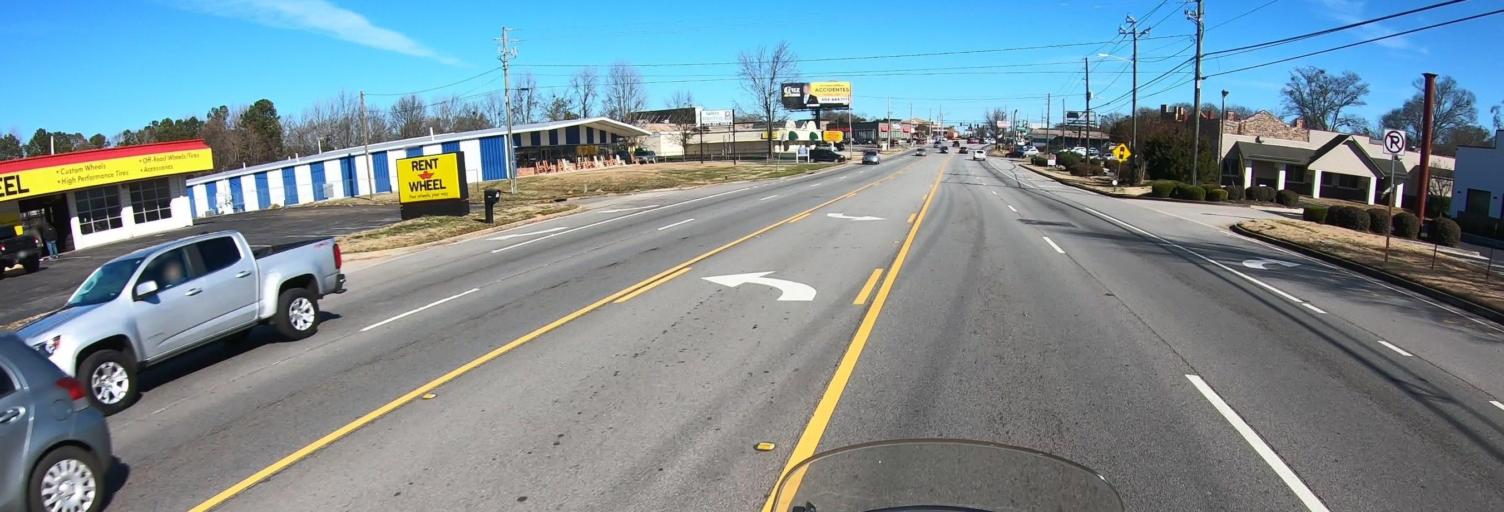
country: US
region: Georgia
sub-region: Hall County
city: Gainesville
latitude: 34.2849
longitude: -83.8452
